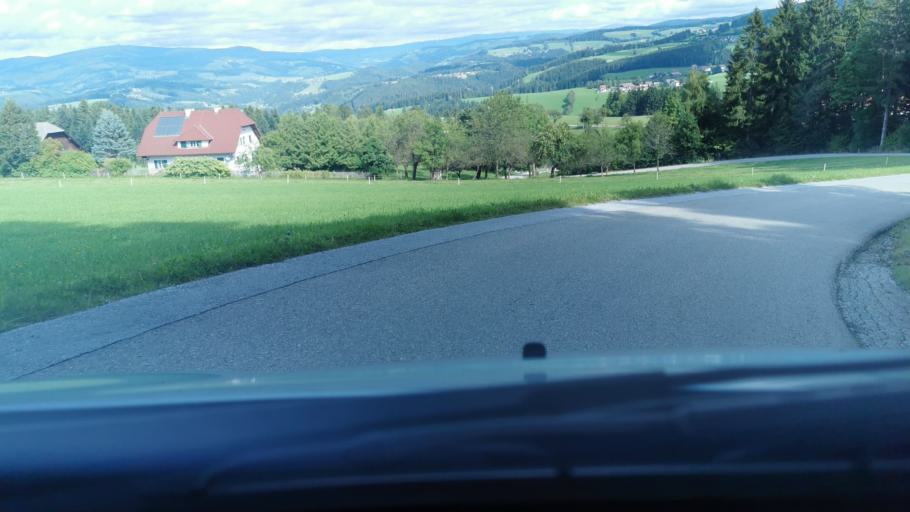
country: AT
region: Styria
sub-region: Politischer Bezirk Weiz
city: Gschaid bei Birkfeld
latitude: 47.3311
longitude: 15.7077
